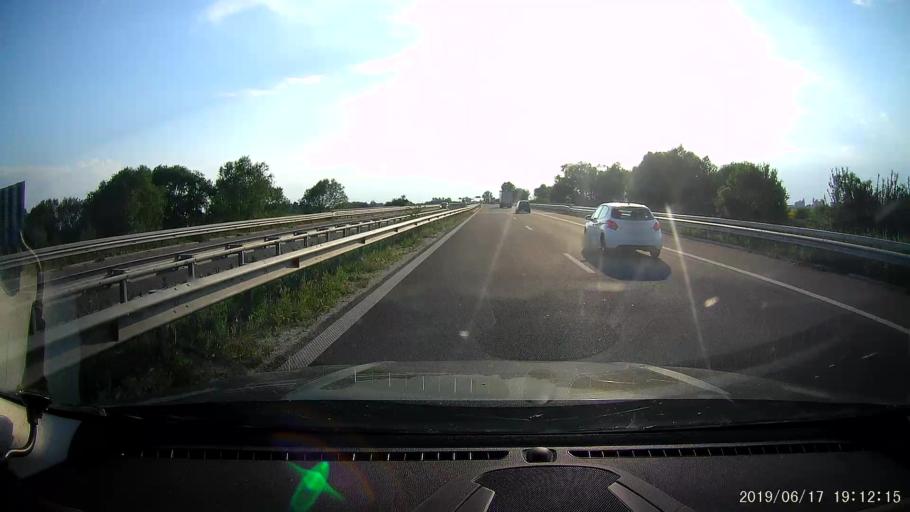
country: BG
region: Plovdiv
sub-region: Obshtina Plovdiv
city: Plovdiv
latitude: 42.2145
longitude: 24.7406
